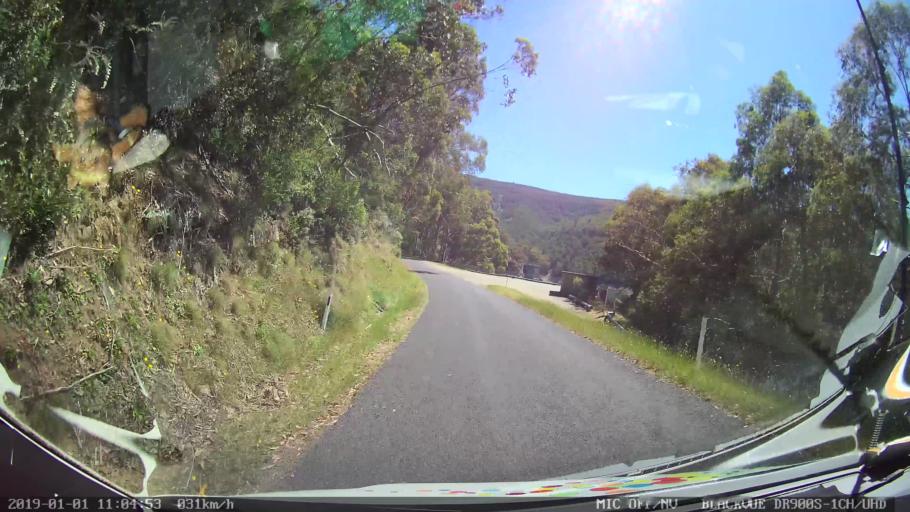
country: AU
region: New South Wales
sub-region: Snowy River
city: Jindabyne
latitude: -35.9681
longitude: 148.3894
